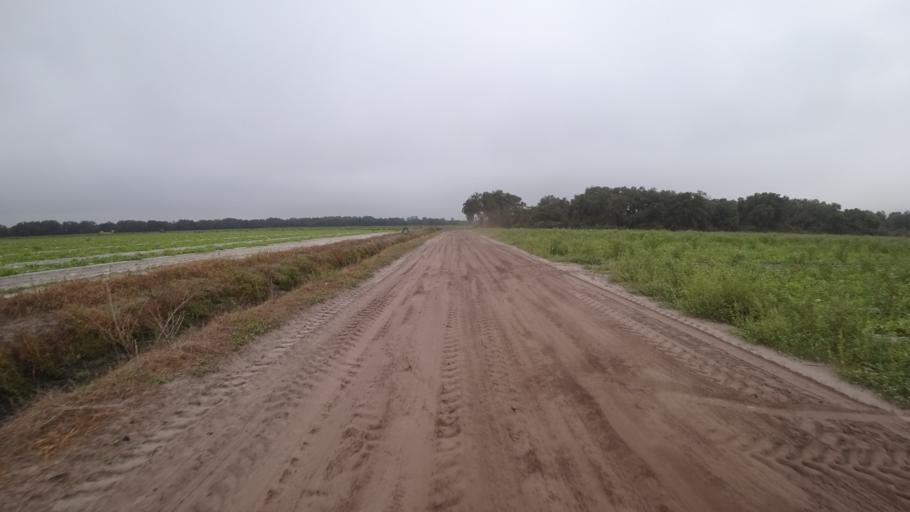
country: US
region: Florida
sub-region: Sarasota County
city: Warm Mineral Springs
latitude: 27.2865
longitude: -82.1583
